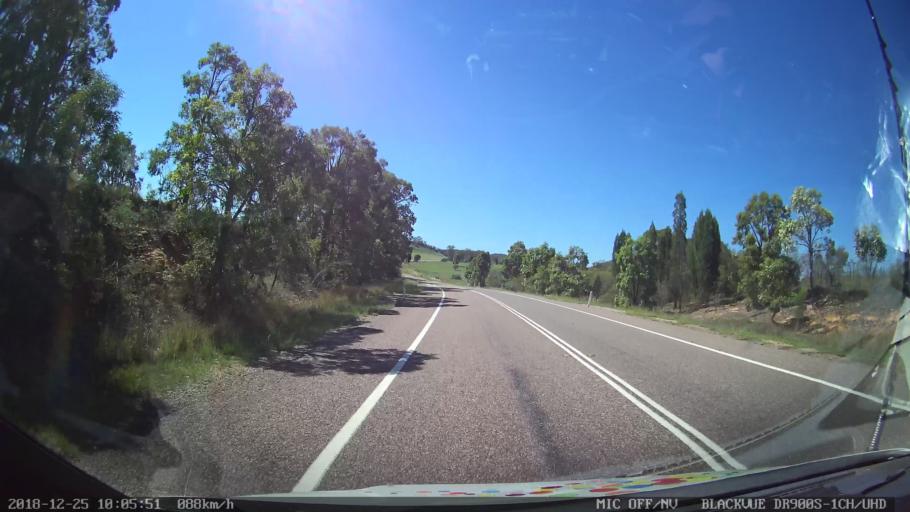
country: AU
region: New South Wales
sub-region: Upper Hunter Shire
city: Merriwa
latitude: -32.2526
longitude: 150.4870
